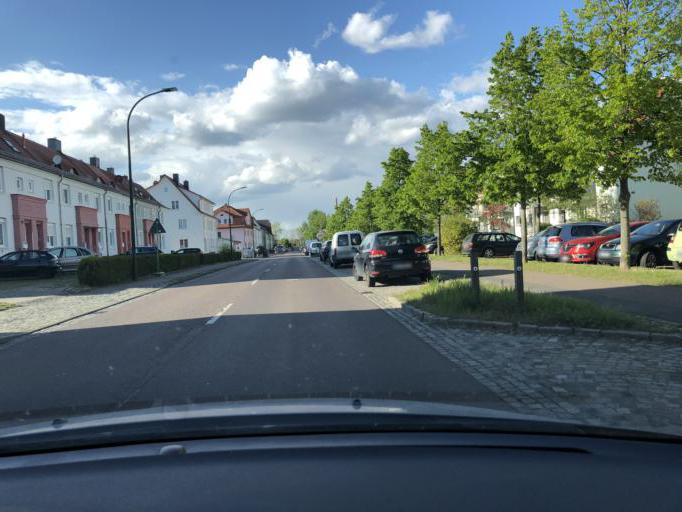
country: DE
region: Saxony
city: Markkleeberg
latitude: 51.2630
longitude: 12.3775
